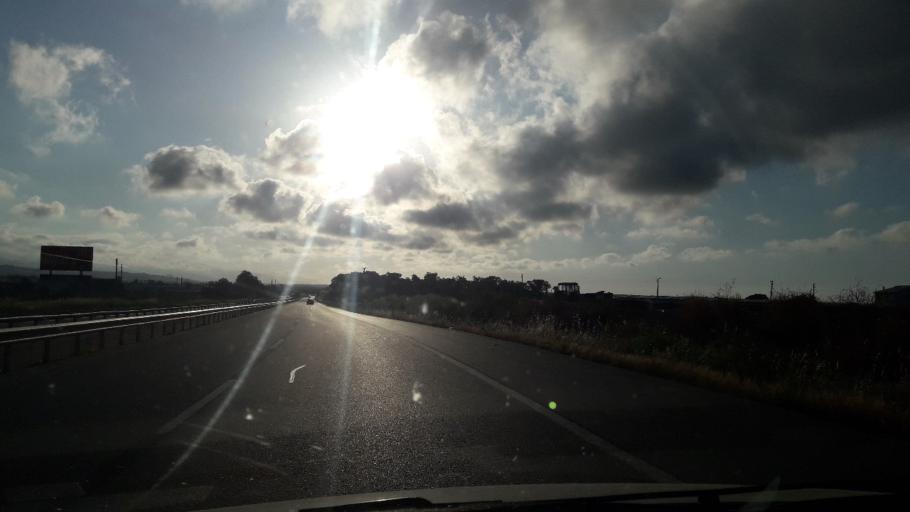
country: TR
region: Samsun
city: Bafra
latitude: 41.6017
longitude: 35.8292
